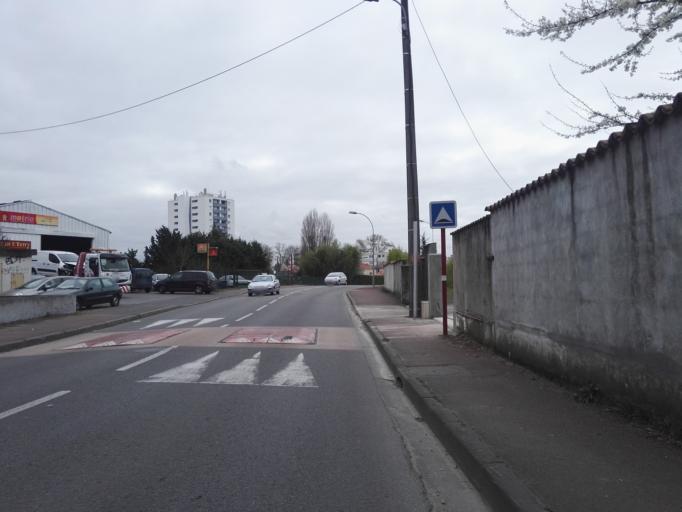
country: FR
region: Aquitaine
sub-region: Departement de la Gironde
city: Talence
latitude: 44.7837
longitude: -0.5779
